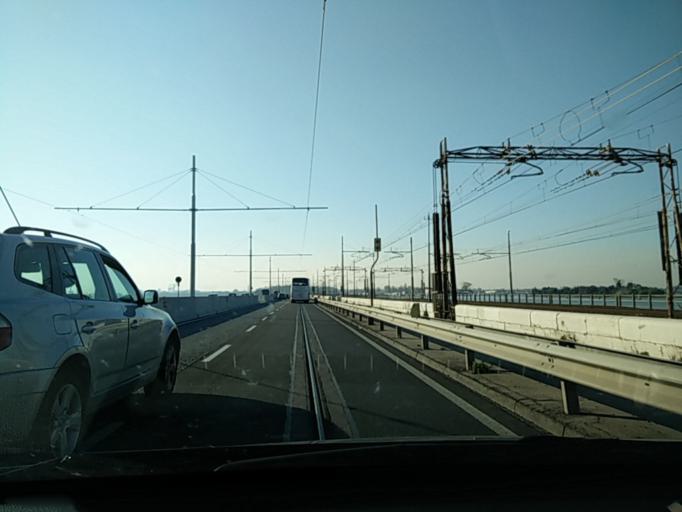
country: IT
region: Veneto
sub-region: Provincia di Venezia
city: Campalto
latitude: 45.4591
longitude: 12.2894
